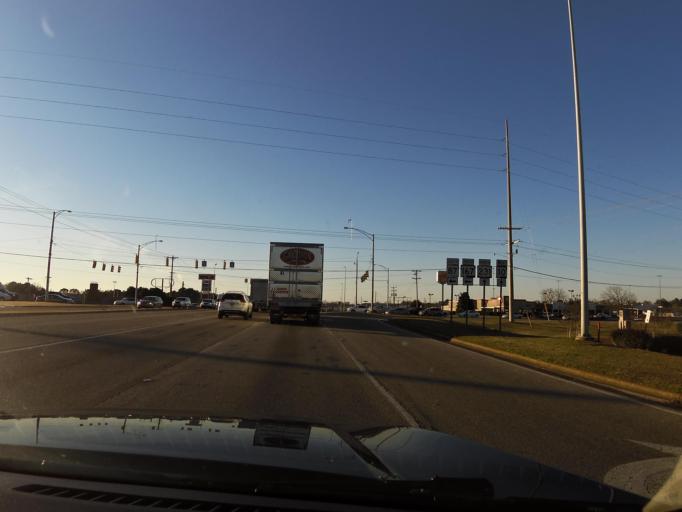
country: US
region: Alabama
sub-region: Pike County
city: Troy
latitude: 31.7856
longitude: -85.9626
